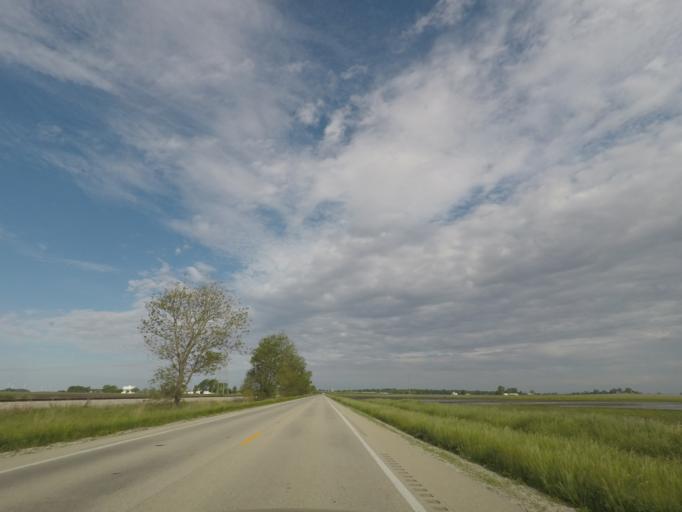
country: US
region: Illinois
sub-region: Logan County
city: Mount Pulaski
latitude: 39.9959
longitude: -89.2574
